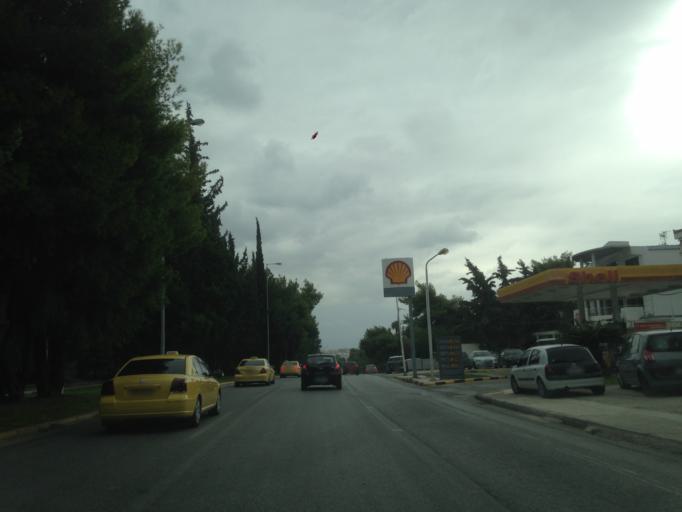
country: GR
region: Attica
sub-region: Nomarchia Anatolikis Attikis
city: Vouliagmeni
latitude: 37.8221
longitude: 23.7755
